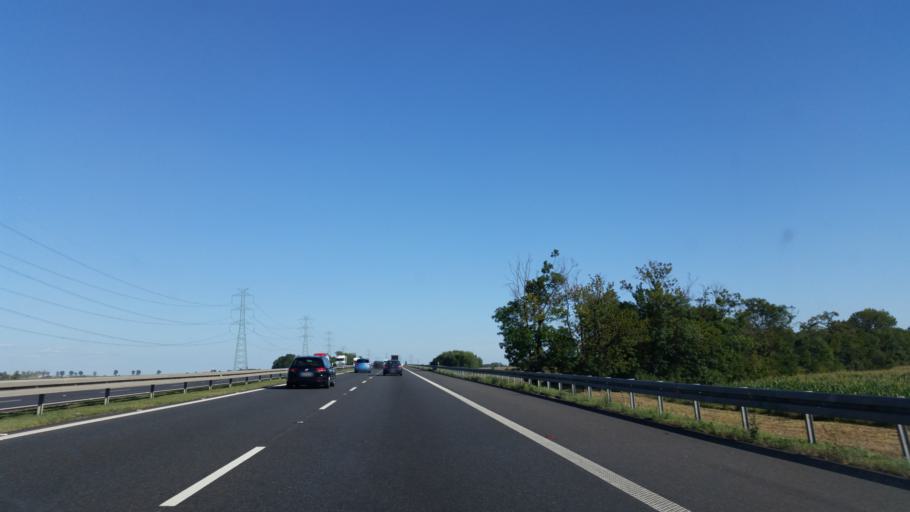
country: PL
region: Lower Silesian Voivodeship
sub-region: Powiat olawski
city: Wierzbno
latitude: 50.9063
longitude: 17.1602
